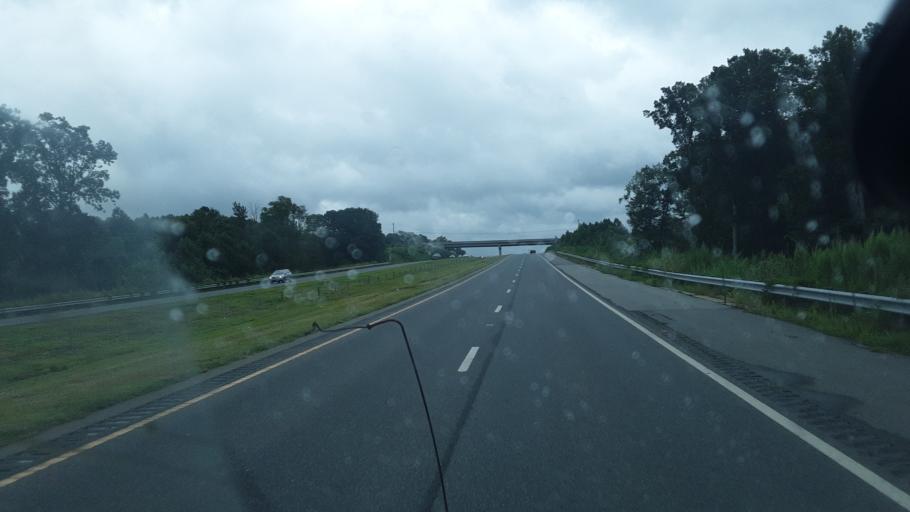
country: US
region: North Carolina
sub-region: Randolph County
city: Randleman
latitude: 35.7986
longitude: -79.8398
